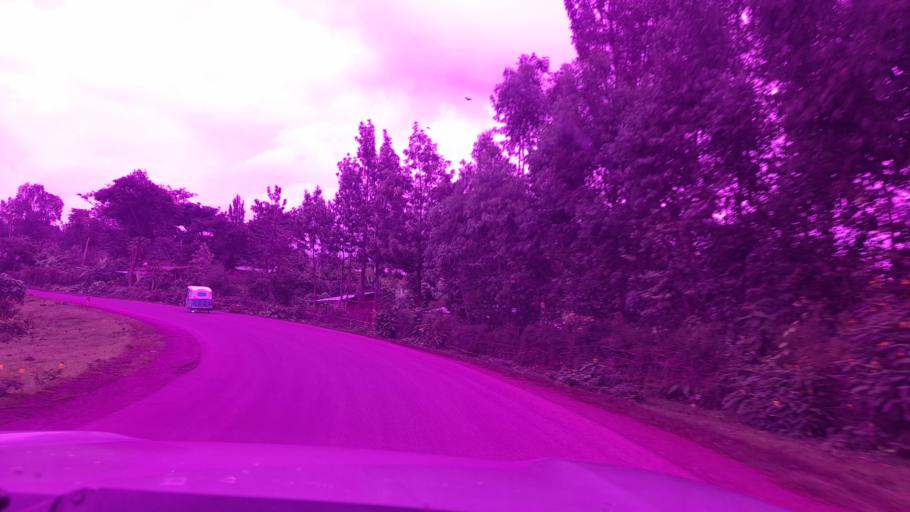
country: ET
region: Oromiya
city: Jima
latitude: 7.9183
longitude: 37.4080
